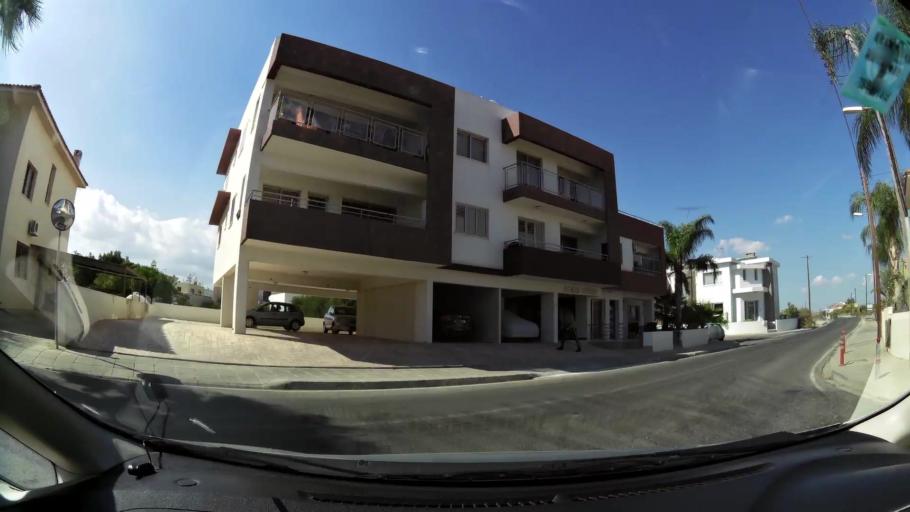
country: CY
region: Larnaka
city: Livadia
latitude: 34.9505
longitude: 33.6215
